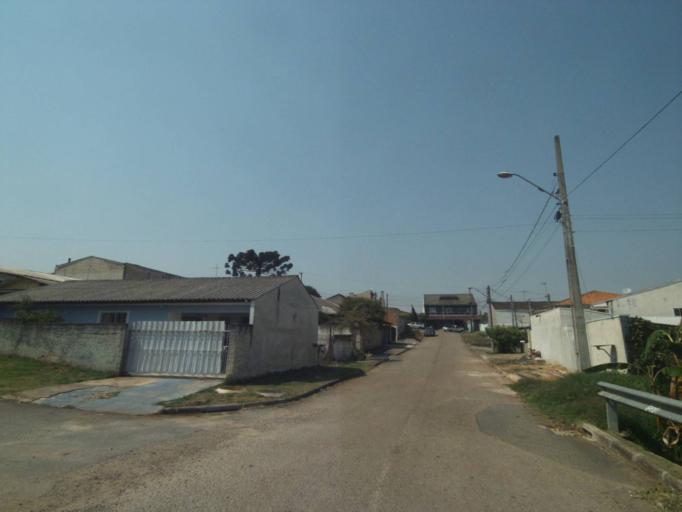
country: BR
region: Parana
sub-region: Sao Jose Dos Pinhais
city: Sao Jose dos Pinhais
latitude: -25.5052
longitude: -49.2681
